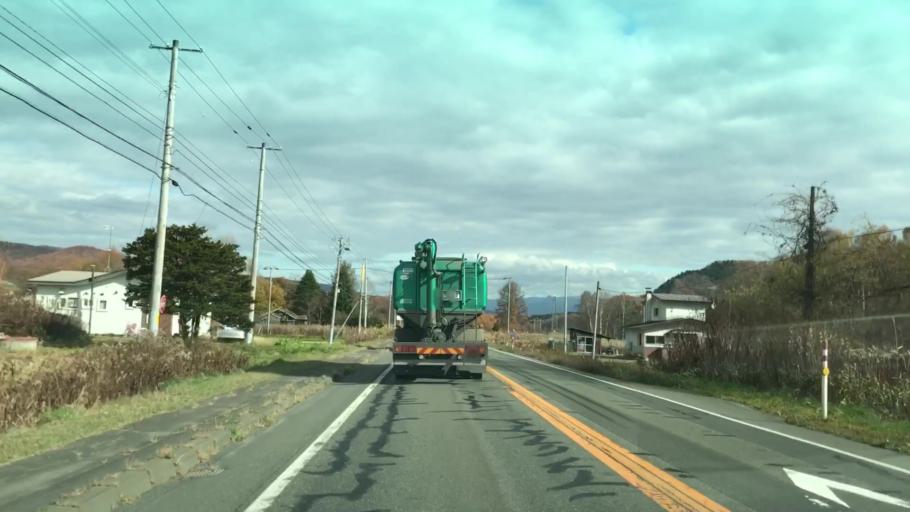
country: JP
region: Hokkaido
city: Shizunai-furukawacho
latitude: 42.7013
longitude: 142.2279
